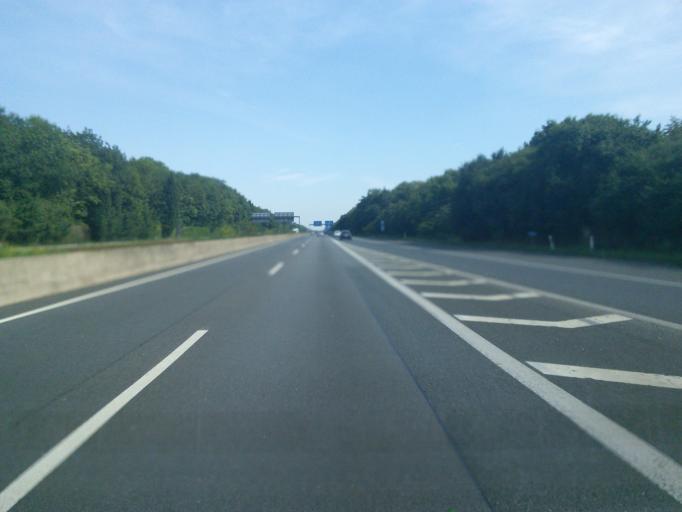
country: DE
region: North Rhine-Westphalia
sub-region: Regierungsbezirk Koln
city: Mengenich
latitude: 51.0046
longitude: 6.8812
